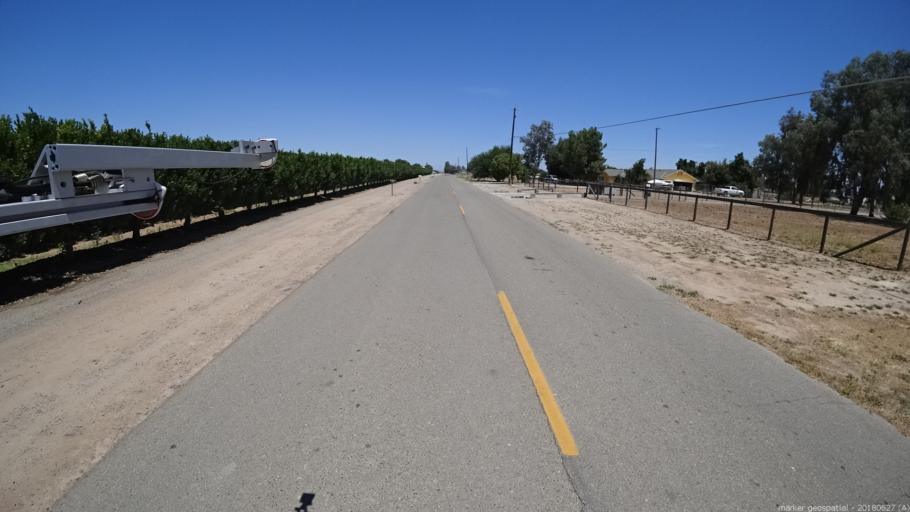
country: US
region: California
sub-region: Madera County
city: Bonadelle Ranchos-Madera Ranchos
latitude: 36.9349
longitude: -119.9214
